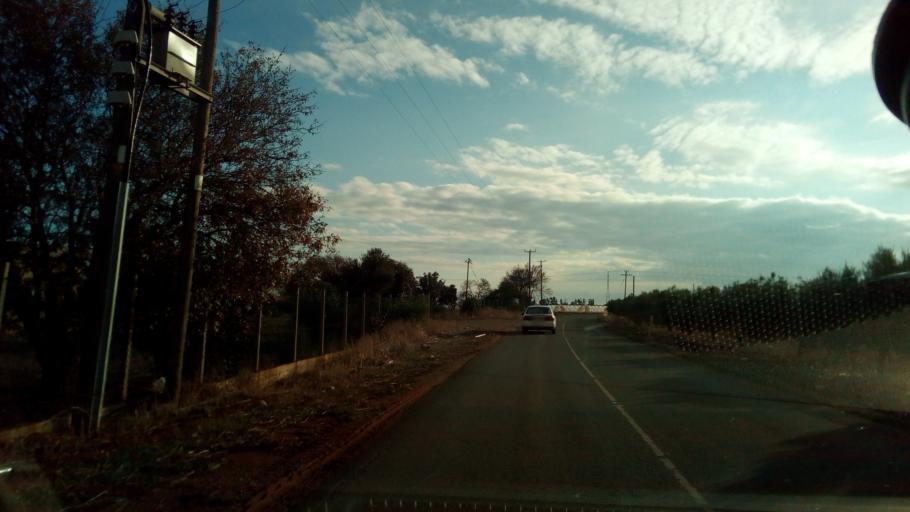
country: CY
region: Ammochostos
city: Avgorou
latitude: 35.0068
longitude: 33.8031
